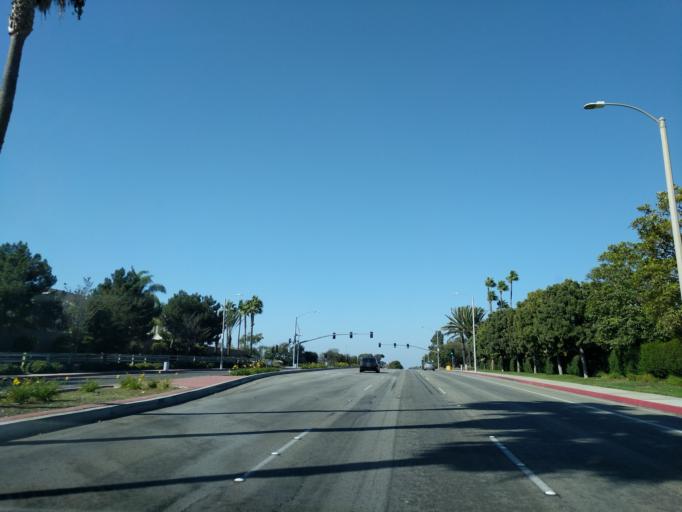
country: US
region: California
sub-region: Orange County
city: Huntington Beach
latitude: 33.6923
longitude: -118.0062
